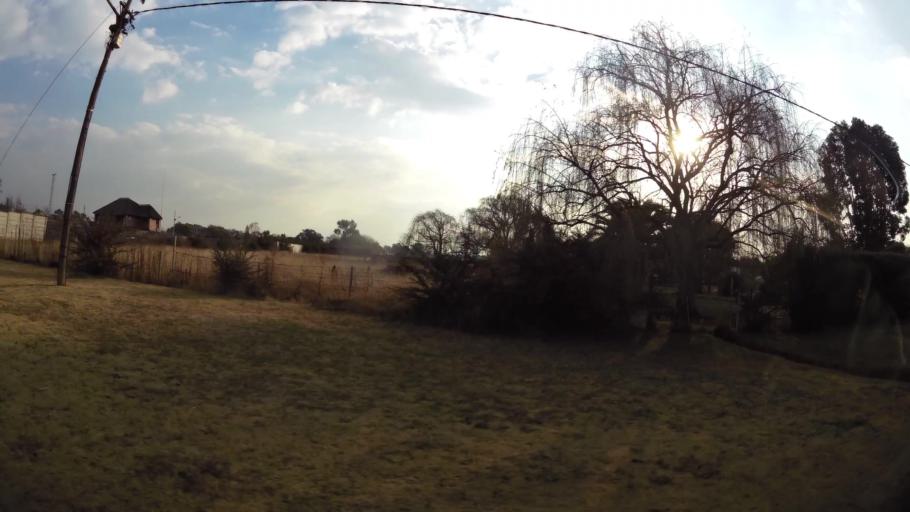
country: ZA
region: Gauteng
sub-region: Ekurhuleni Metropolitan Municipality
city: Benoni
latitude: -26.1232
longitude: 28.3040
